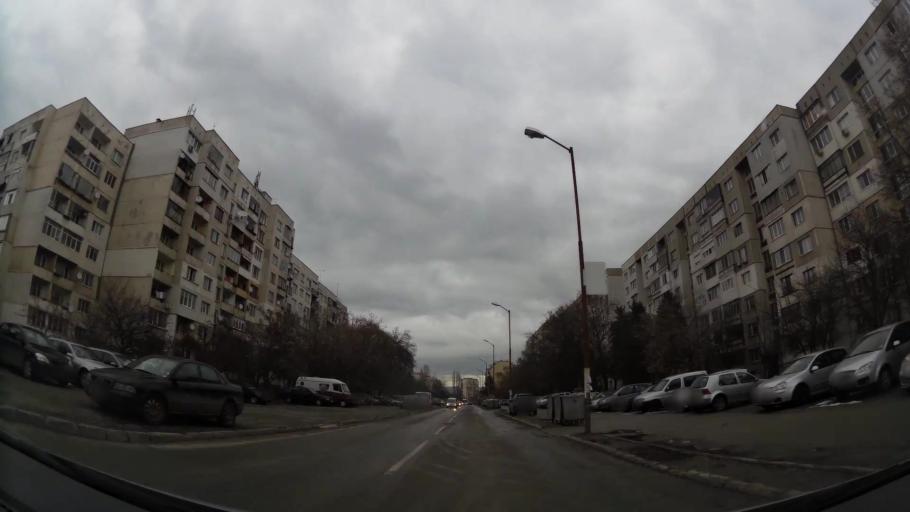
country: BG
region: Sofia-Capital
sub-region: Stolichna Obshtina
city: Sofia
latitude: 42.7273
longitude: 23.2901
